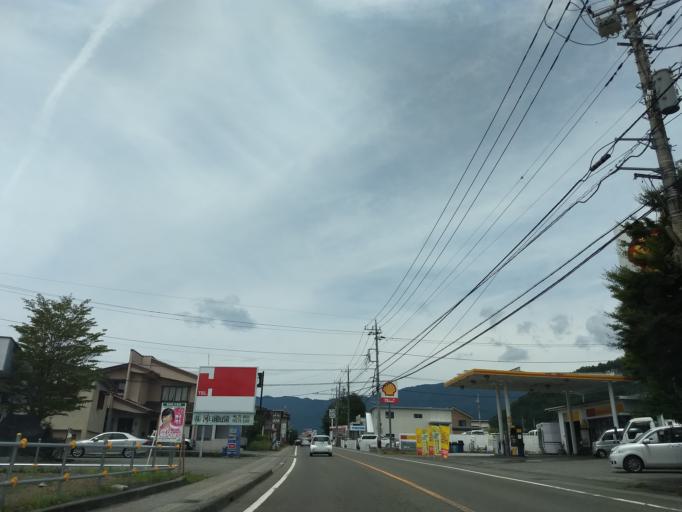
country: JP
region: Yamanashi
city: Fujikawaguchiko
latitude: 35.4962
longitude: 138.7752
